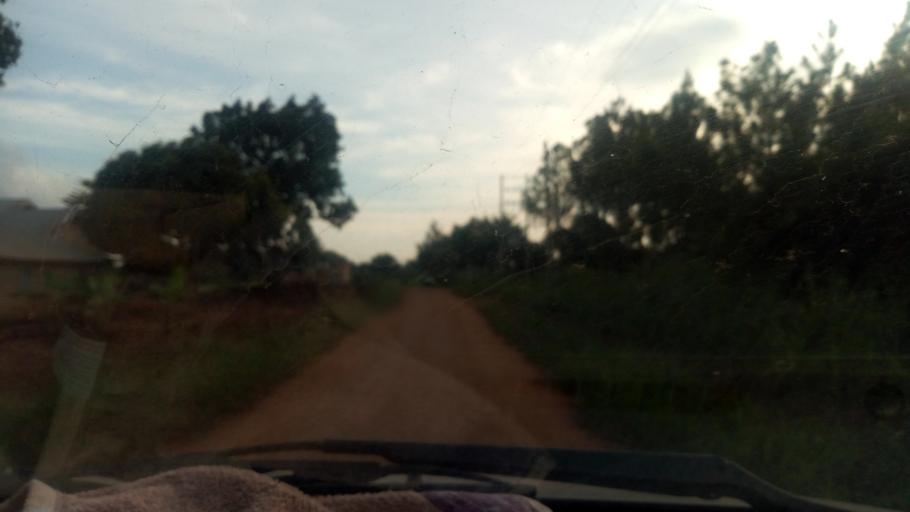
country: UG
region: Western Region
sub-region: Kiryandongo District
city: Kiryandongo
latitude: 1.8047
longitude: 32.0058
